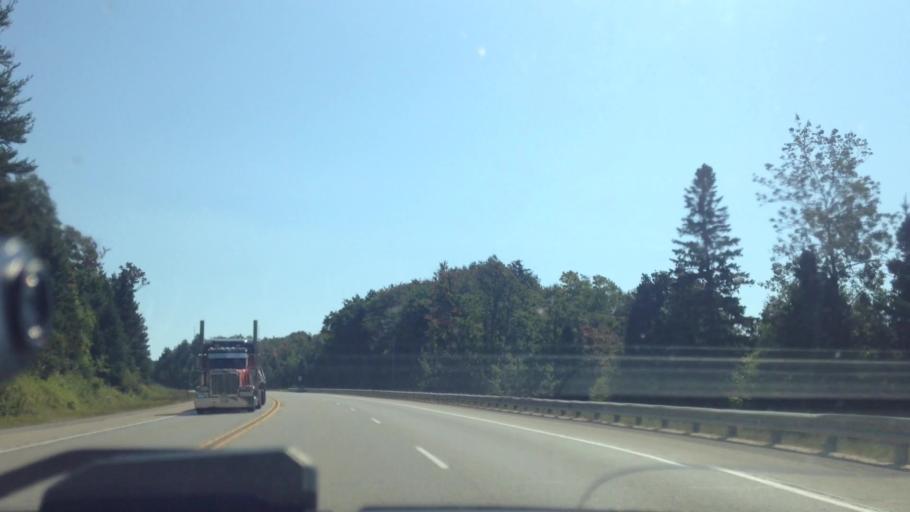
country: US
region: Michigan
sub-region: Alger County
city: Munising
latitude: 46.3904
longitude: -86.6469
